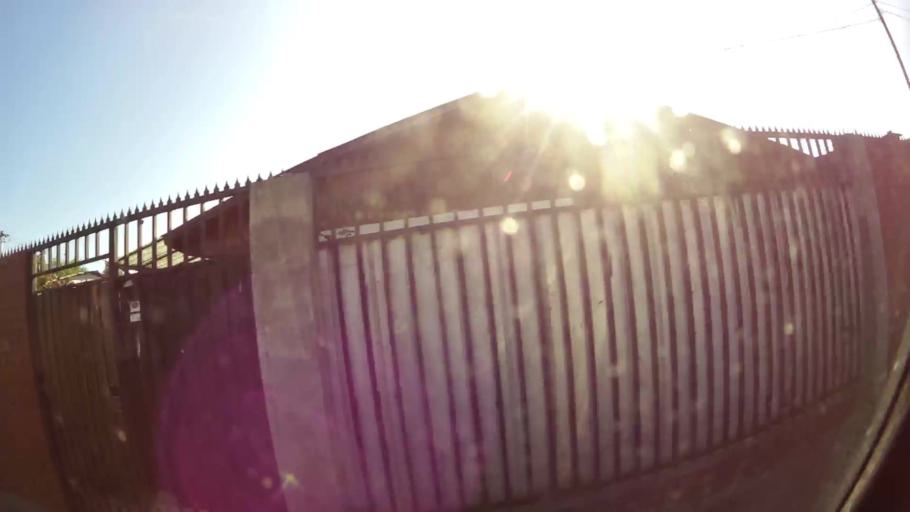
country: CL
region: Santiago Metropolitan
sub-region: Provincia de Santiago
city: Lo Prado
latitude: -33.4890
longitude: -70.7645
